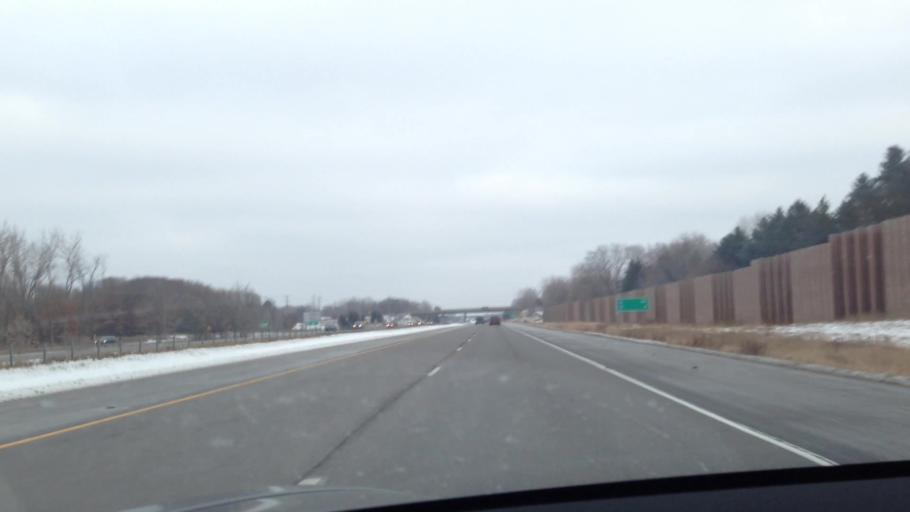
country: US
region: Minnesota
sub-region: Anoka County
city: Circle Pines
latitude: 45.1666
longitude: -93.1490
